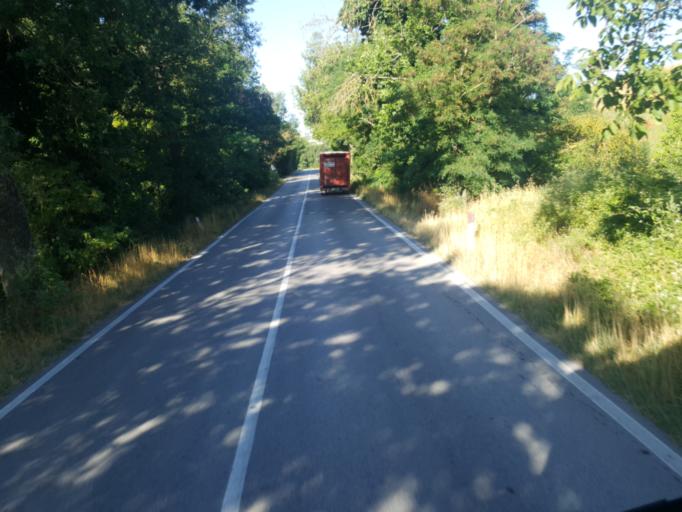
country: IT
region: The Marches
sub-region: Provincia di Pesaro e Urbino
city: Montecalvo in Foglia
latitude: 43.7914
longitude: 12.6440
